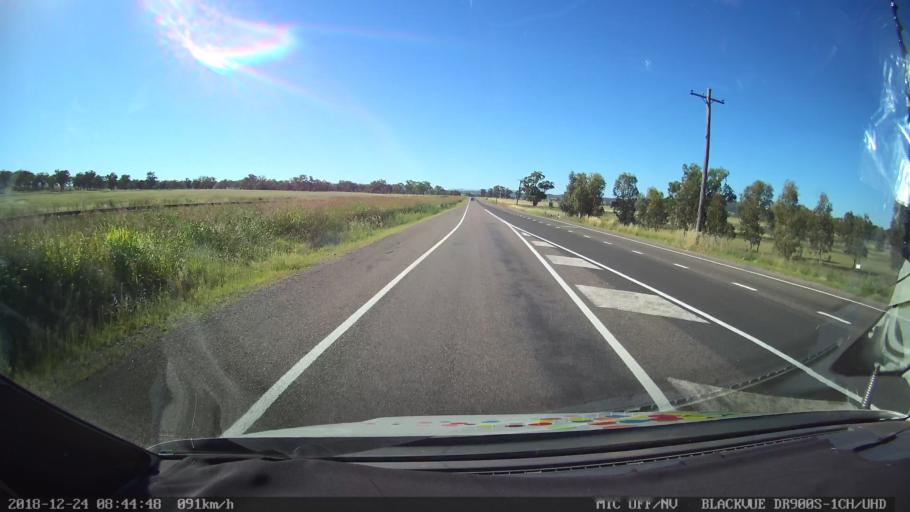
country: AU
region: New South Wales
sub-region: Liverpool Plains
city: Quirindi
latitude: -31.4065
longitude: 150.6497
